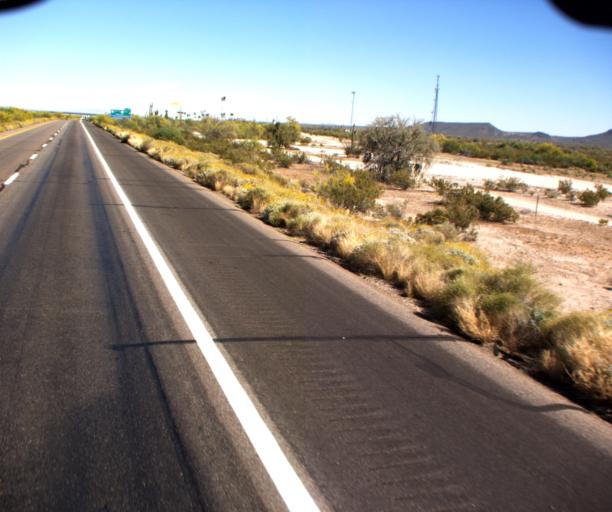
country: US
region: Arizona
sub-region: Pinal County
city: Maricopa
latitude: 32.8346
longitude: -112.1414
